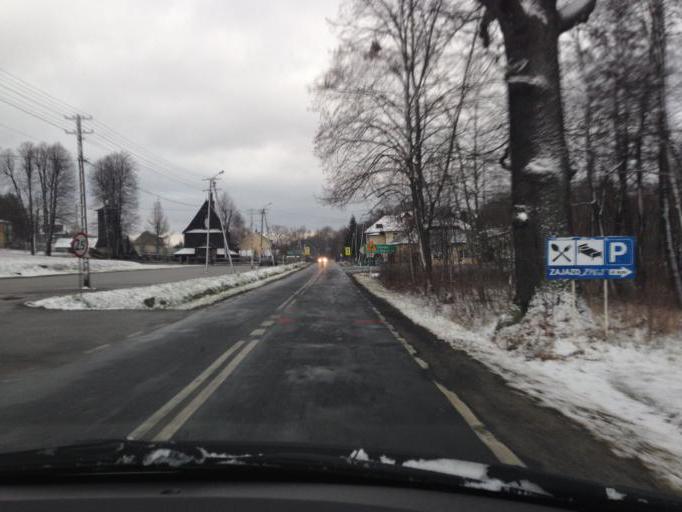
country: PL
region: Lesser Poland Voivodeship
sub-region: Powiat brzeski
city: Gnojnik
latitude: 49.8514
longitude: 20.6187
